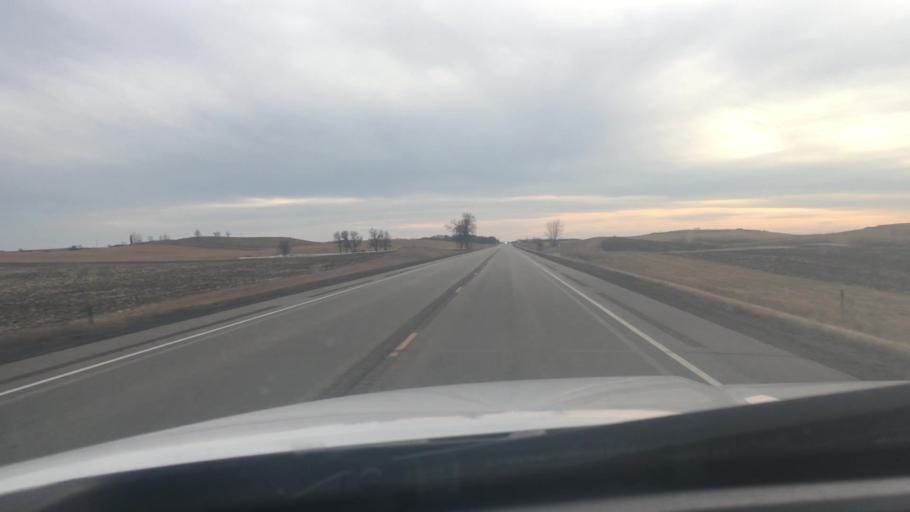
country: US
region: Minnesota
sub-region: Otter Tail County
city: Perham
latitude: 46.3434
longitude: -95.7185
